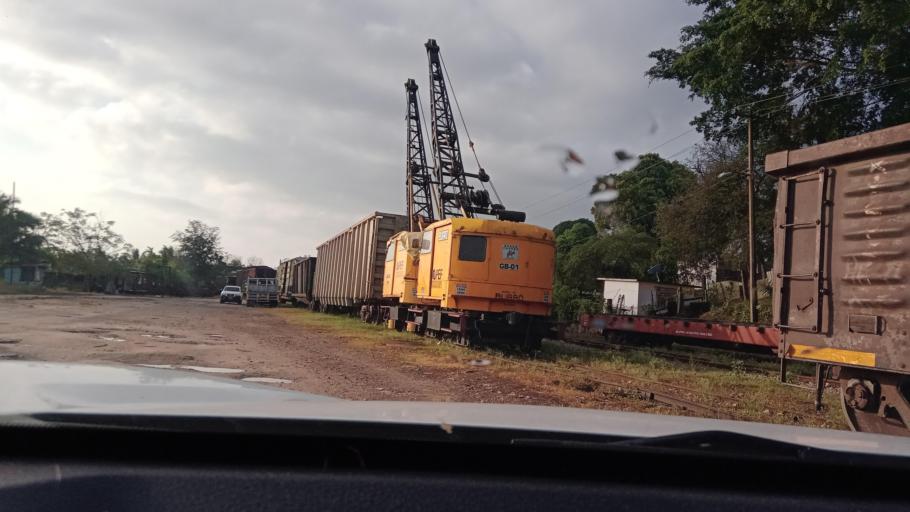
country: MX
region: Veracruz
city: Las Choapas
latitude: 17.8794
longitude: -94.0965
